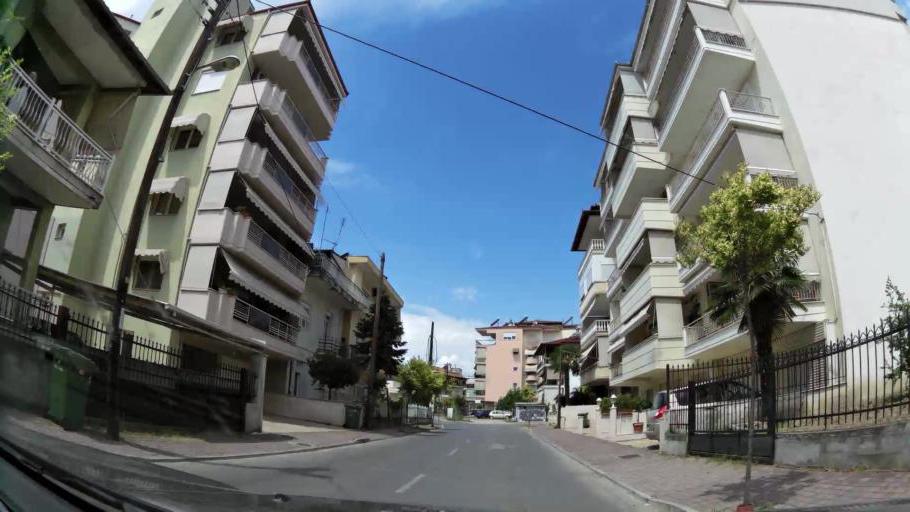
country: GR
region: Central Macedonia
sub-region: Nomos Pierias
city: Katerini
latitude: 40.2683
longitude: 22.5021
